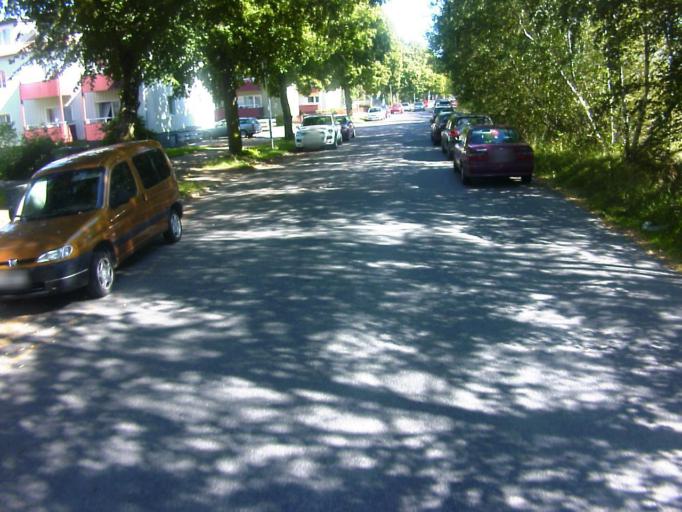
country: SE
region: Soedermanland
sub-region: Eskilstuna Kommun
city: Eskilstuna
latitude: 59.3801
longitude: 16.5156
